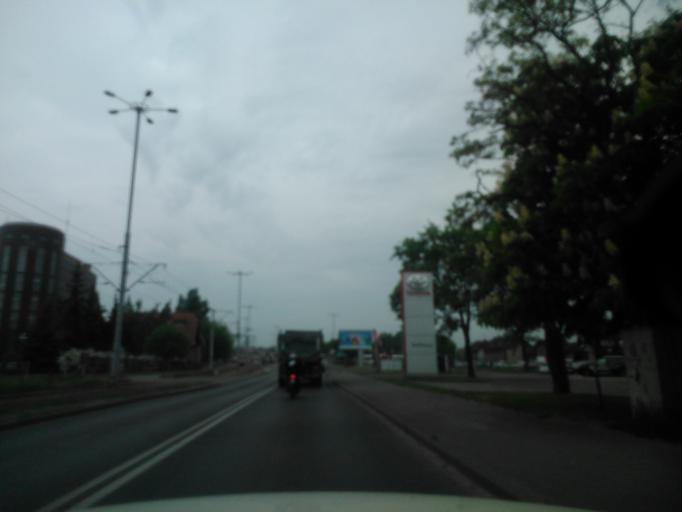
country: PL
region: Kujawsko-Pomorskie
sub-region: Torun
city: Torun
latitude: 53.0262
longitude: 18.6357
